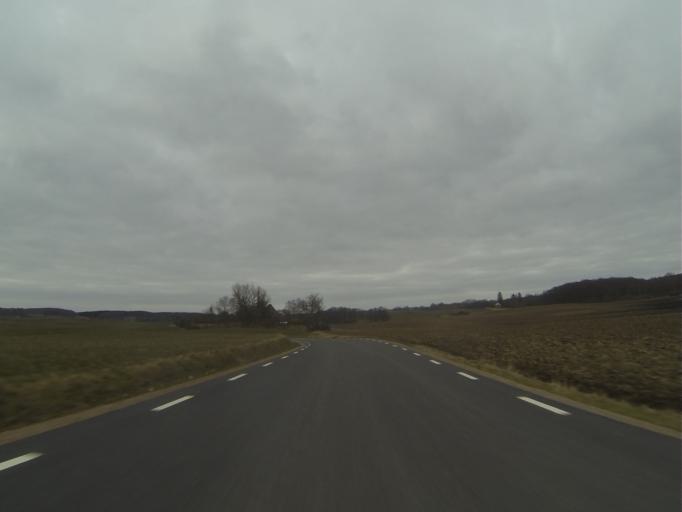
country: SE
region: Skane
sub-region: Skurups Kommun
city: Skurup
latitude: 55.5368
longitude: 13.4431
